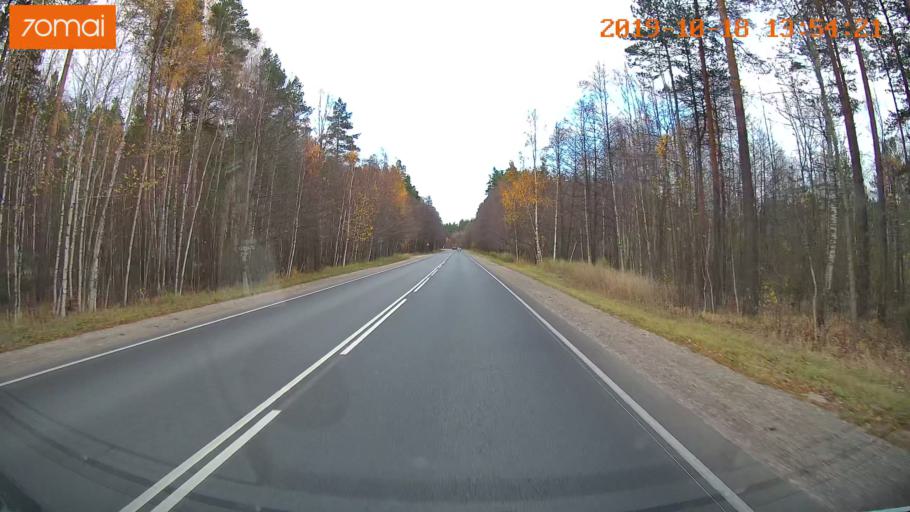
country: RU
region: Rjazan
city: Spas-Klepiki
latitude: 55.0414
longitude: 40.0066
